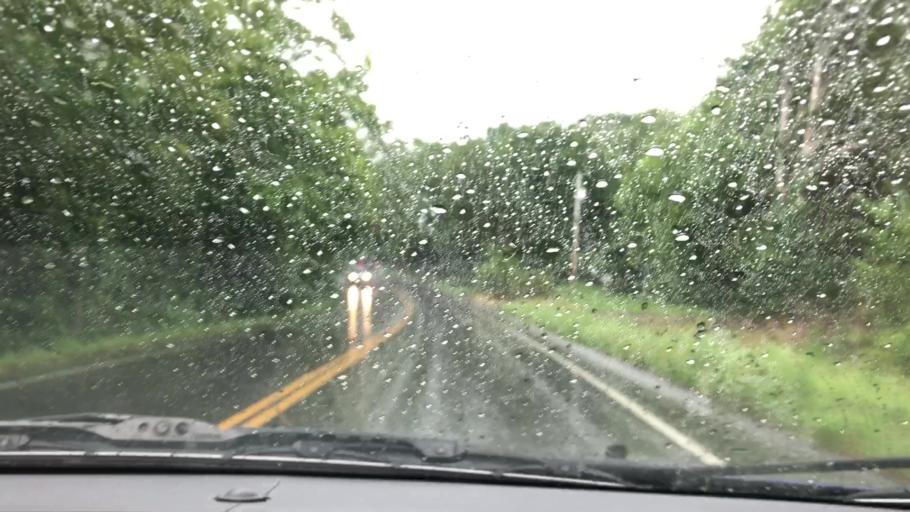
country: US
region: Tennessee
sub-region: Williamson County
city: Franklin
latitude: 35.9031
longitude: -86.9111
